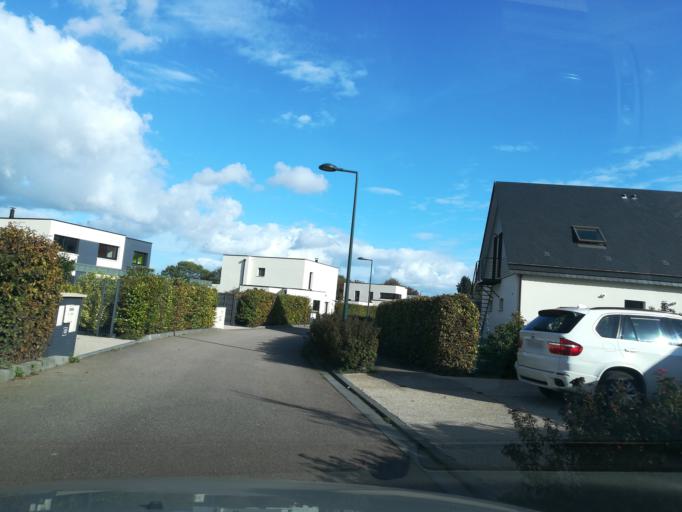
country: FR
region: Haute-Normandie
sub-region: Departement de la Seine-Maritime
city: Bois-Guillaume
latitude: 49.4748
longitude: 1.1300
